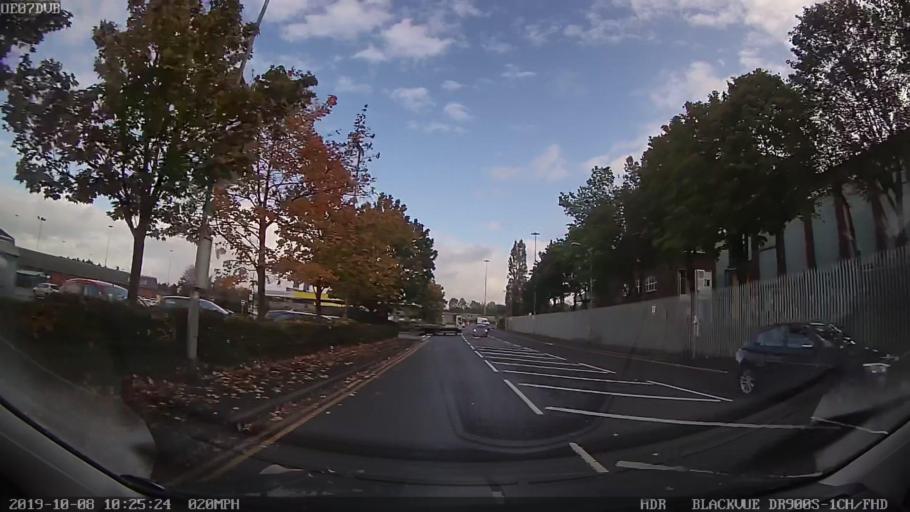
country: GB
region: England
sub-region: Manchester
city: Failsworth
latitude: 53.5209
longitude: -2.1530
